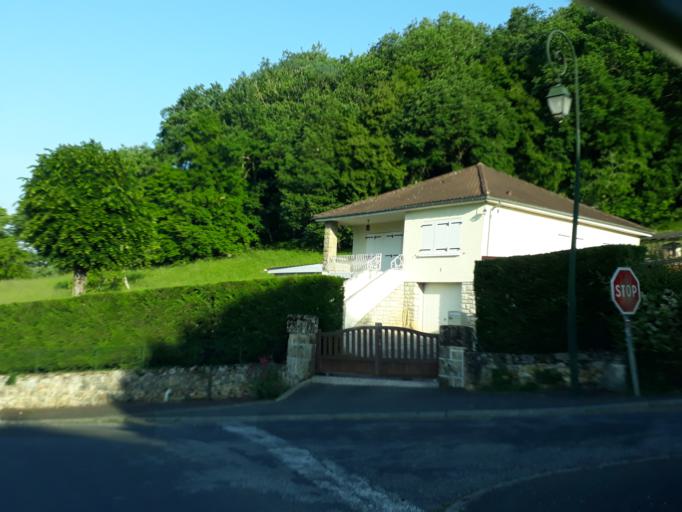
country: FR
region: Limousin
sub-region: Departement de la Correze
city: Saint-Pantaleon-de-Larche
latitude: 45.1042
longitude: 1.4619
